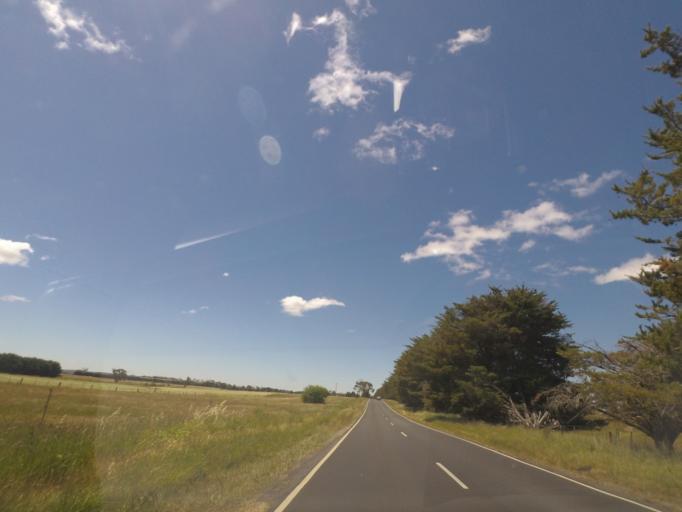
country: AU
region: Victoria
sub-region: Mount Alexander
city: Castlemaine
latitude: -37.2485
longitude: 144.3213
